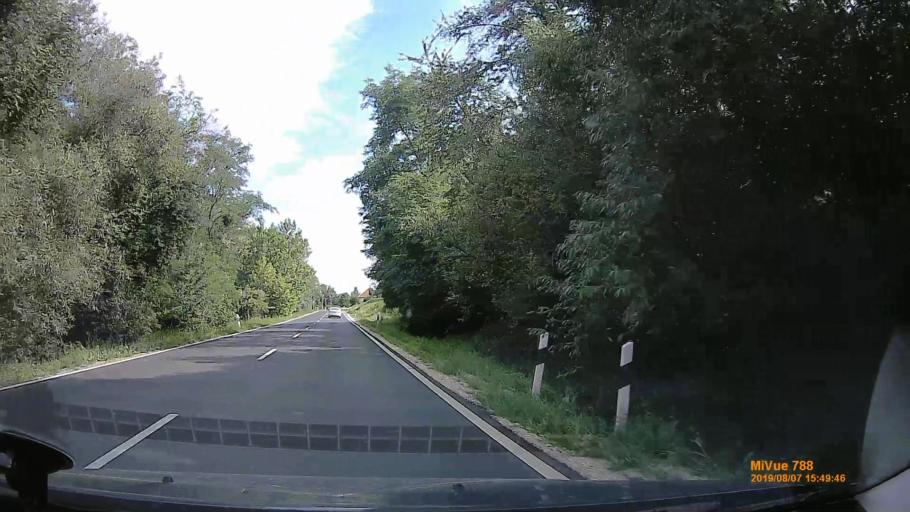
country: HU
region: Vas
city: Jak
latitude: 47.1466
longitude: 16.6448
